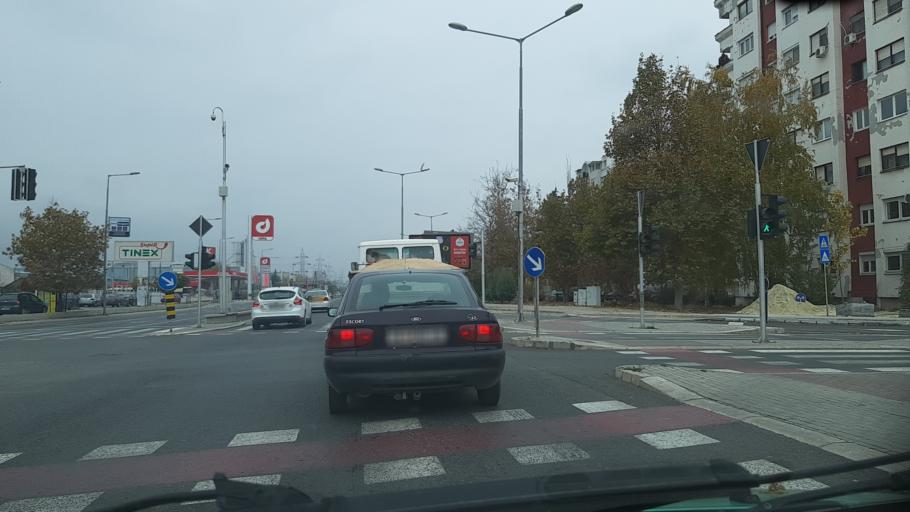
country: MK
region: Kisela Voda
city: Usje
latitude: 41.9822
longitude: 21.4542
